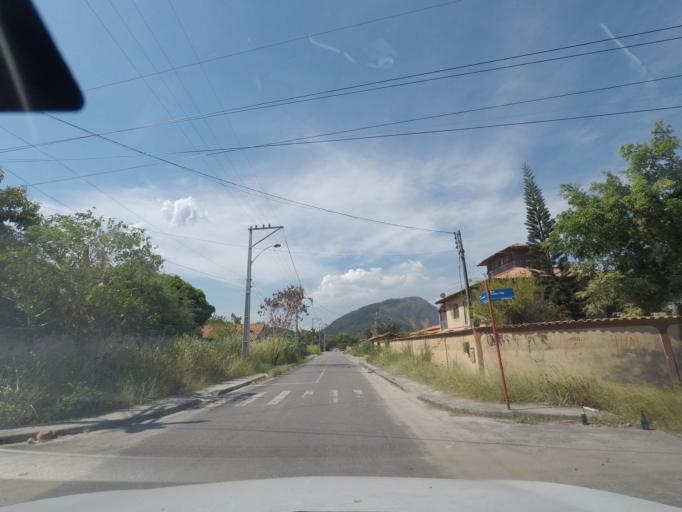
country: BR
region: Rio de Janeiro
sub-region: Marica
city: Marica
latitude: -22.9622
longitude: -42.9676
